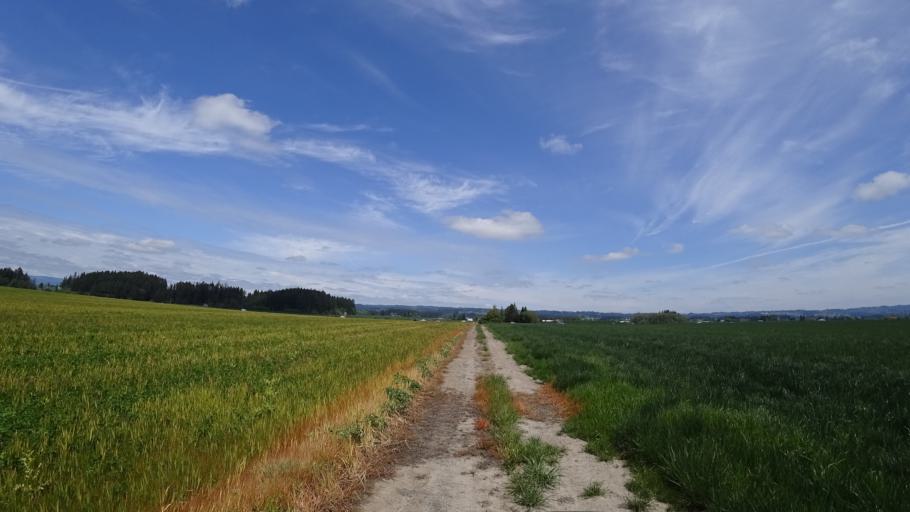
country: US
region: Oregon
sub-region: Washington County
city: North Plains
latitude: 45.5669
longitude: -122.9432
